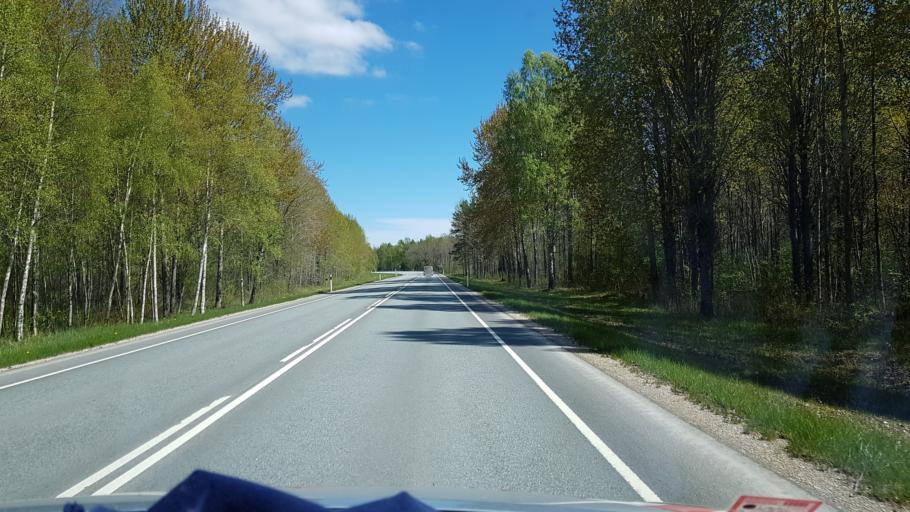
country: EE
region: Saare
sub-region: Kuressaare linn
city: Kuressaare
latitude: 58.3131
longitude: 22.6087
